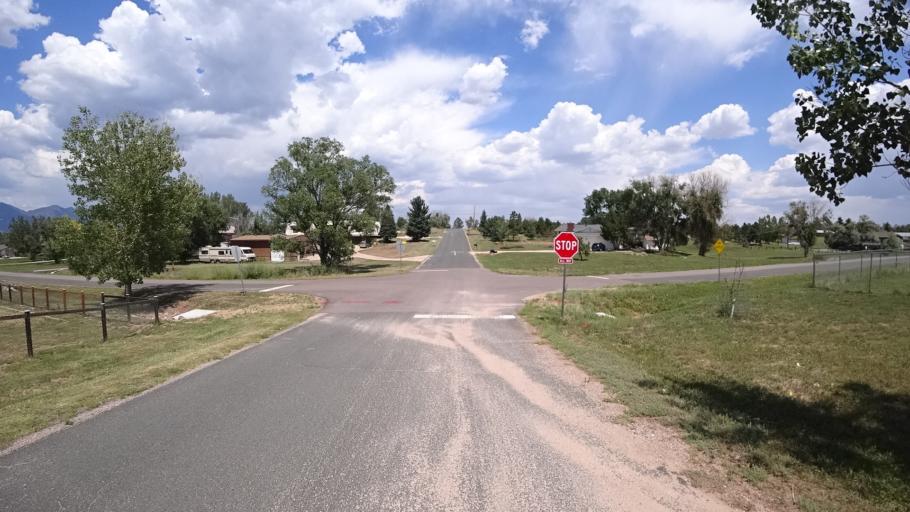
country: US
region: Colorado
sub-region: El Paso County
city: Air Force Academy
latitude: 38.9364
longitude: -104.8032
